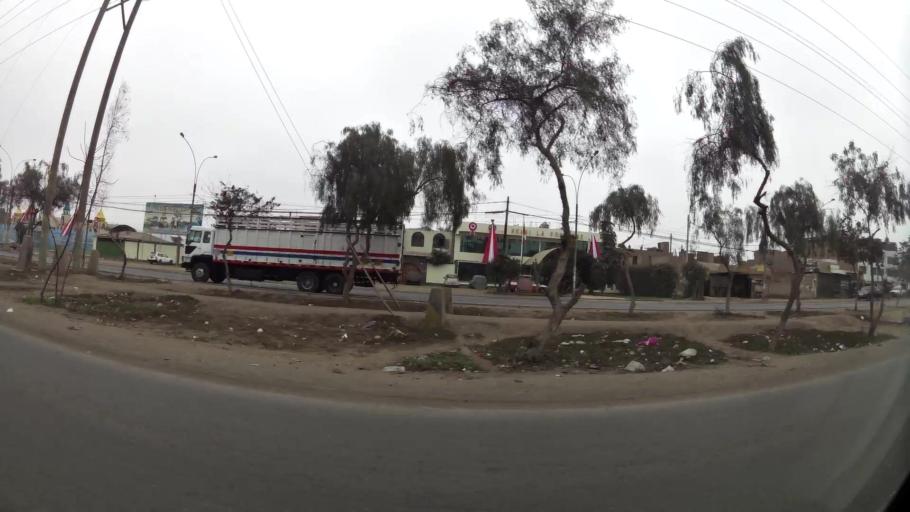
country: PE
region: Lima
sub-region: Lima
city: Urb. Santo Domingo
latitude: -11.9261
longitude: -77.0639
